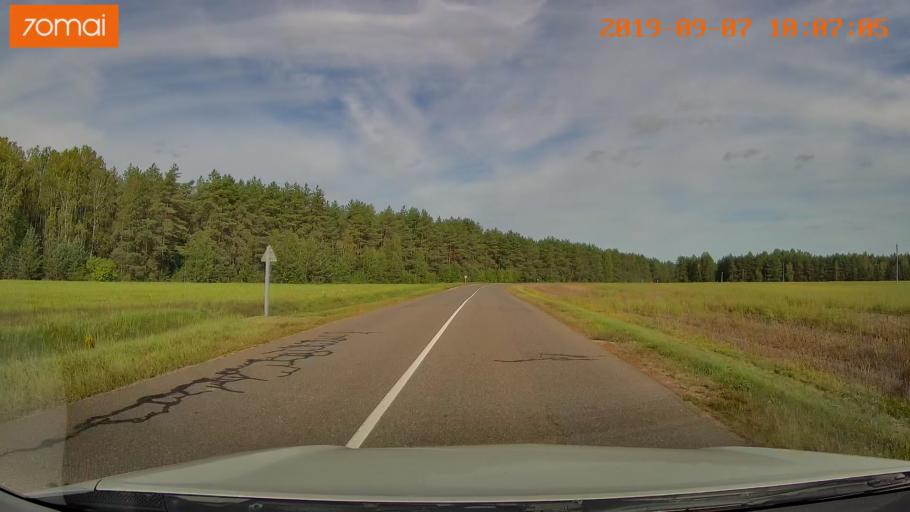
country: BY
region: Grodnenskaya
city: Voranava
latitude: 54.0706
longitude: 25.3964
